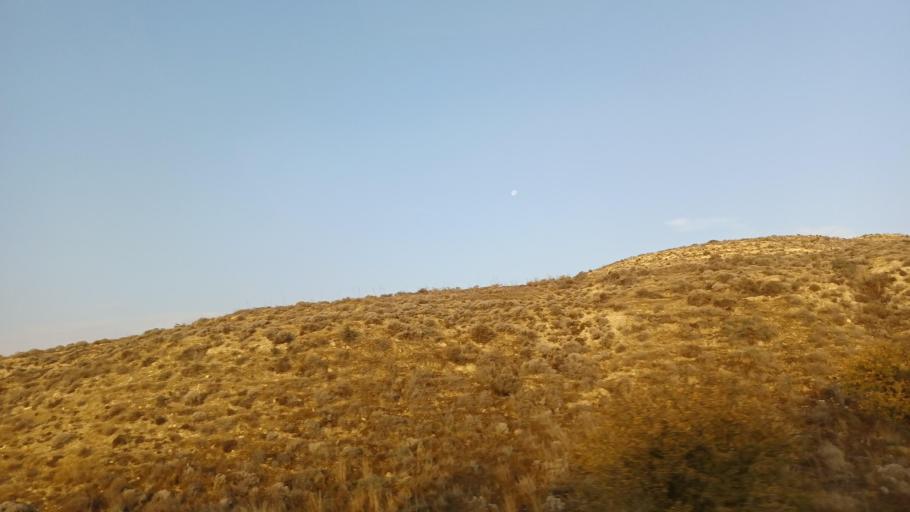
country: CY
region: Larnaka
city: Athienou
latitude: 35.0089
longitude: 33.5276
